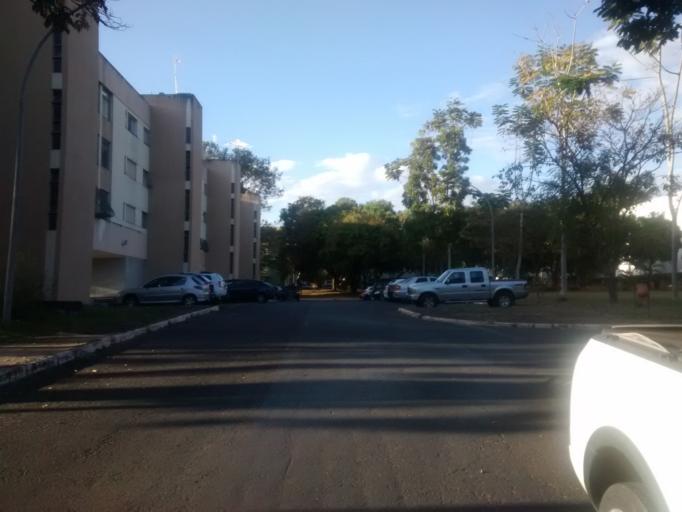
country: BR
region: Federal District
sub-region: Brasilia
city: Brasilia
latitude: -15.7491
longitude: -47.8820
